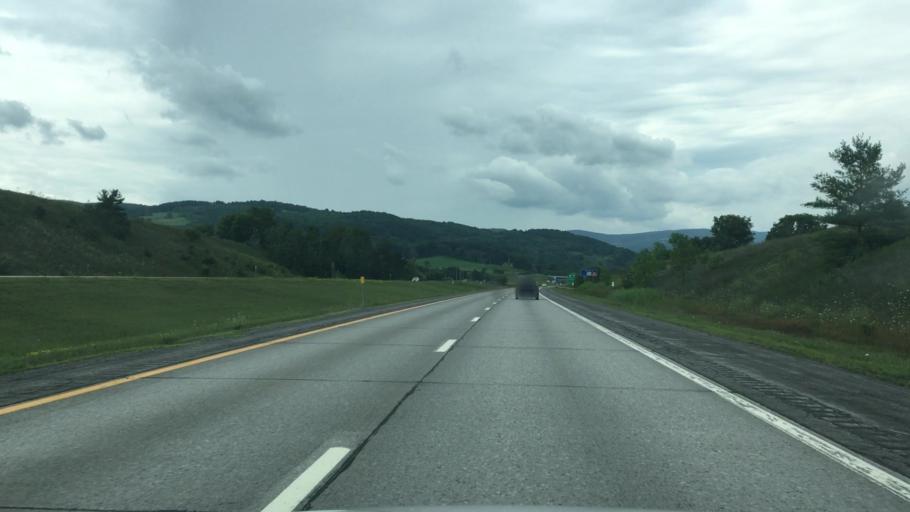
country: US
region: New York
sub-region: Schoharie County
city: Cobleskill
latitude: 42.6608
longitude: -74.4990
